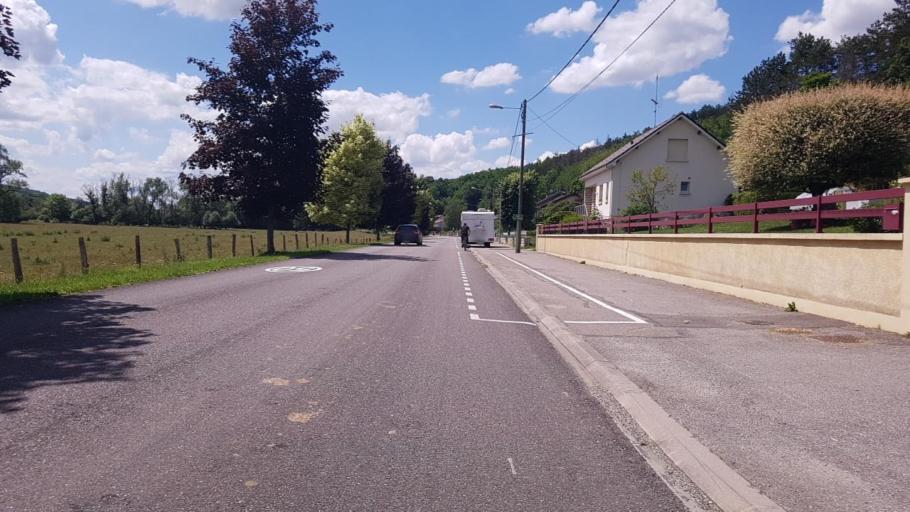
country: FR
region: Lorraine
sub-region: Departement de la Meuse
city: Vacon
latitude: 48.6812
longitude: 5.6117
